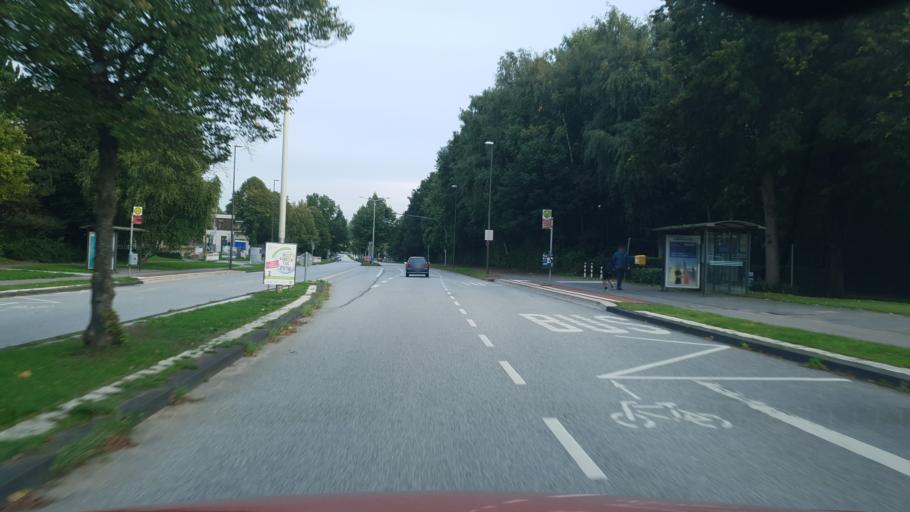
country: DE
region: Schleswig-Holstein
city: Kronshagen
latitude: 54.3451
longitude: 10.1077
